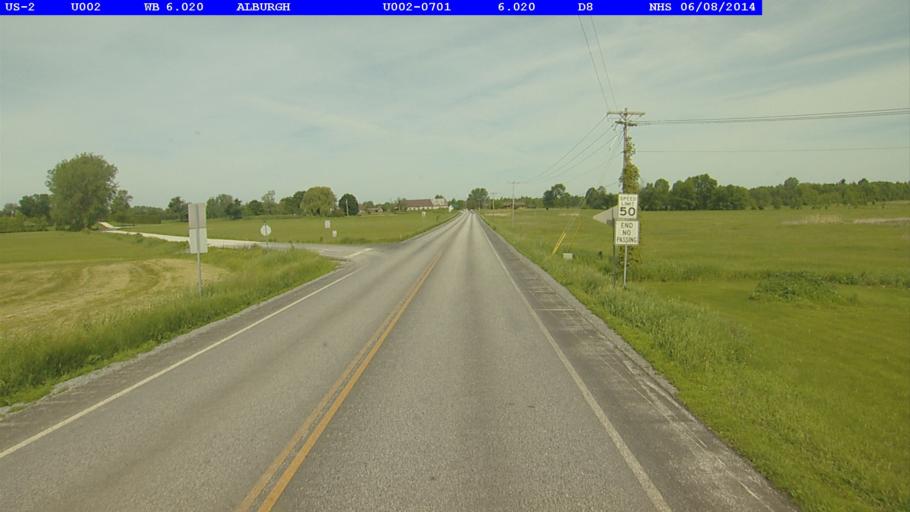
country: US
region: New York
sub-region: Clinton County
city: Rouses Point
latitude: 44.9622
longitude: -73.2806
